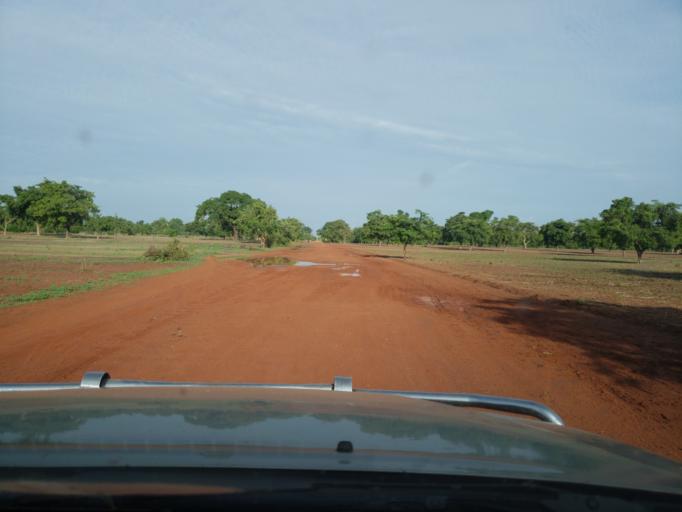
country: ML
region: Sikasso
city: Koutiala
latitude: 12.4195
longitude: -5.7005
